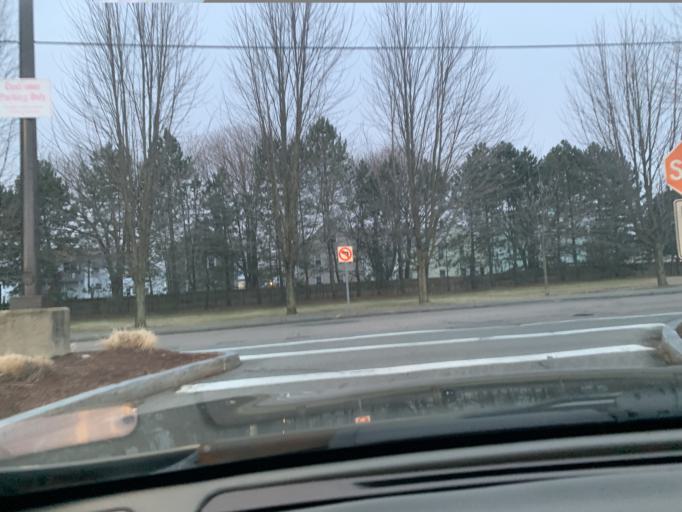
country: US
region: Massachusetts
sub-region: Norfolk County
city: Quincy
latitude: 42.2717
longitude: -71.0282
